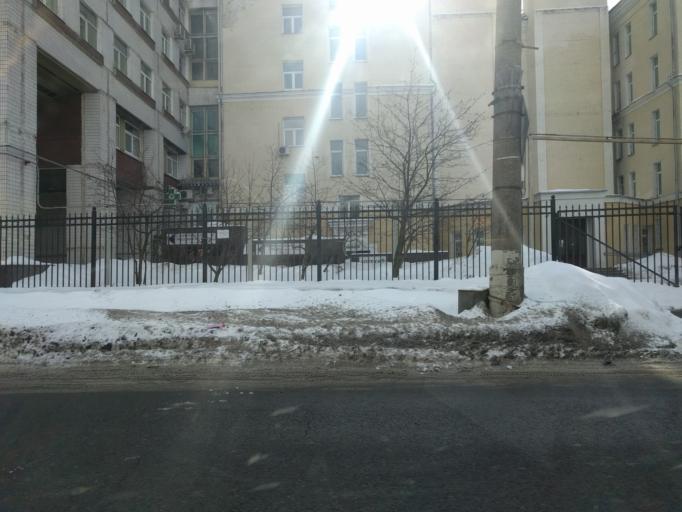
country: RU
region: Moscow
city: Metrogorodok
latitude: 55.8024
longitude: 37.7802
